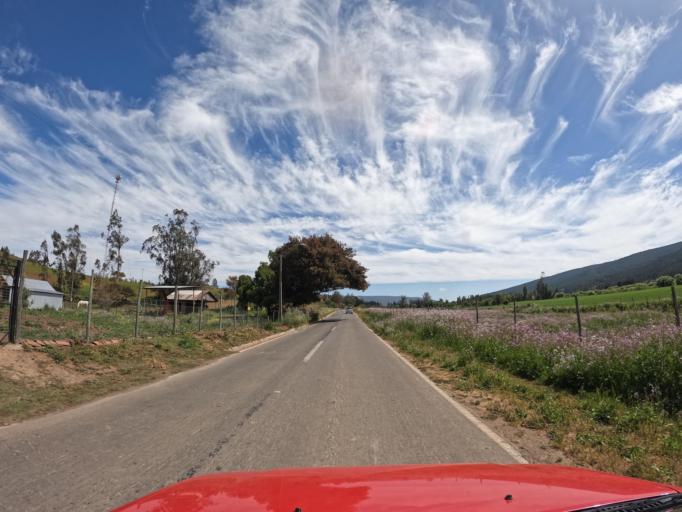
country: CL
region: Maule
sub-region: Provincia de Talca
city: Constitucion
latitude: -35.0074
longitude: -72.0325
